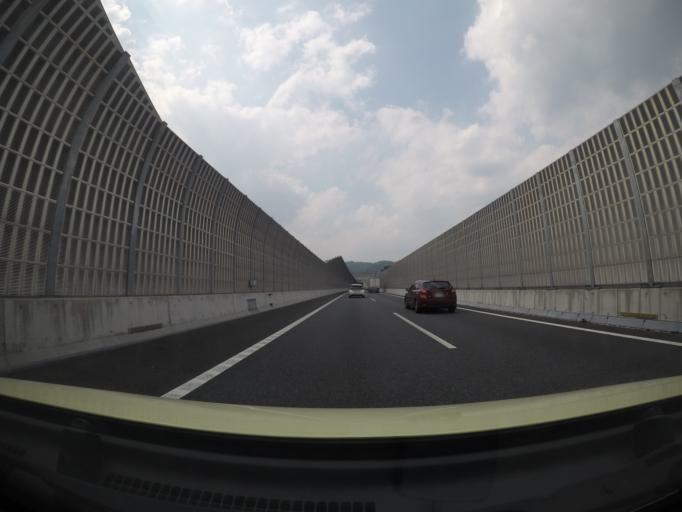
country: JP
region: Tokyo
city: Hachioji
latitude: 35.5856
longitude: 139.2902
